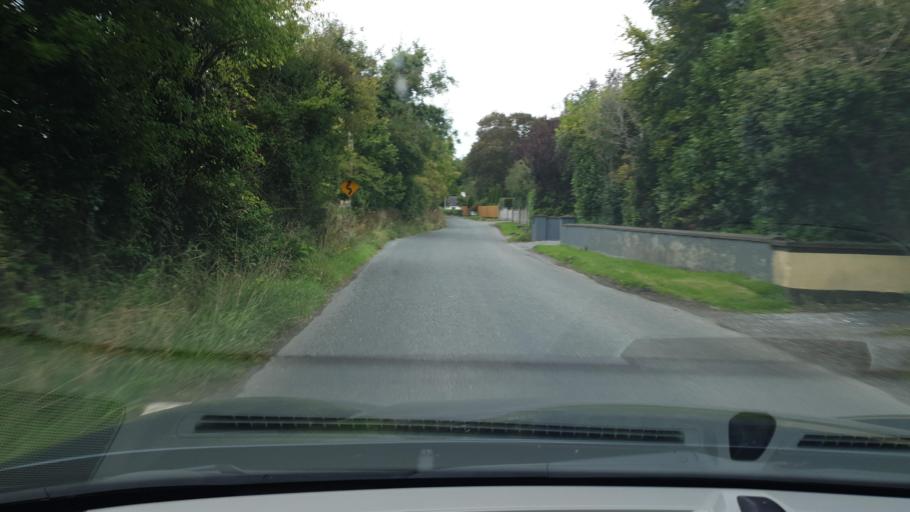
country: IE
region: Leinster
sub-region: Kildare
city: Kilcock
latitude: 53.4024
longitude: -6.6619
